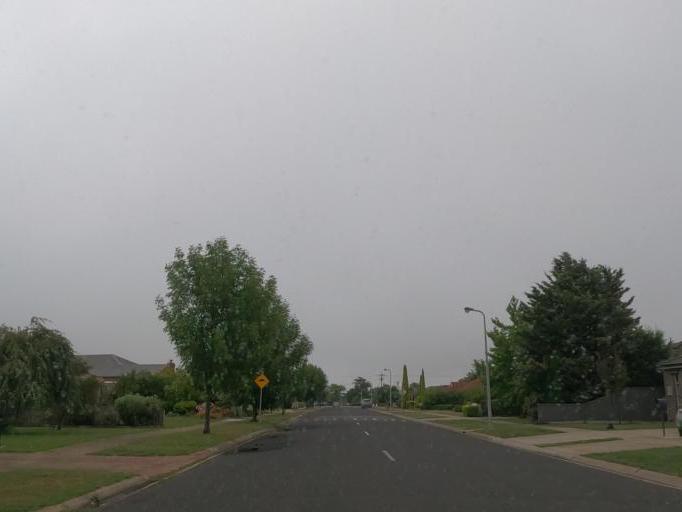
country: AU
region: Victoria
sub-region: Ballarat North
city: Newington
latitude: -37.5479
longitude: 143.7946
